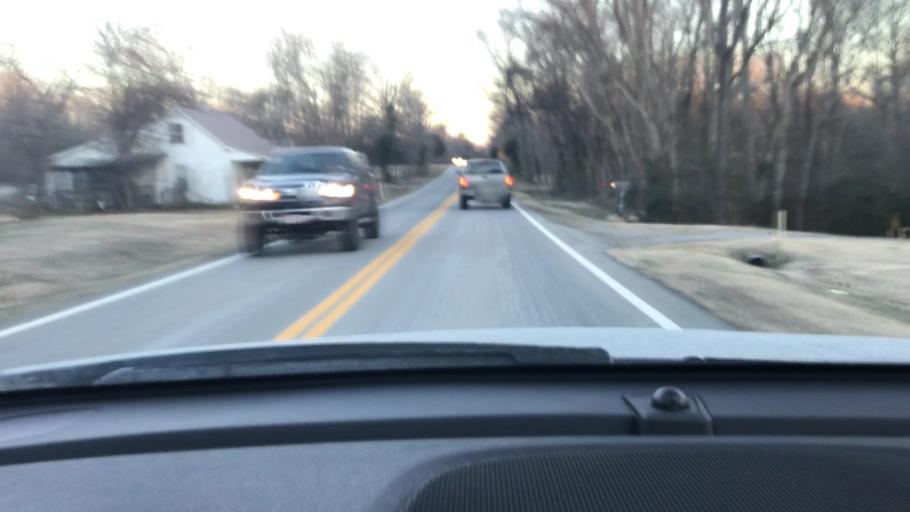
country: US
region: Tennessee
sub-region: Dickson County
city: Charlotte
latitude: 36.2144
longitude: -87.2613
